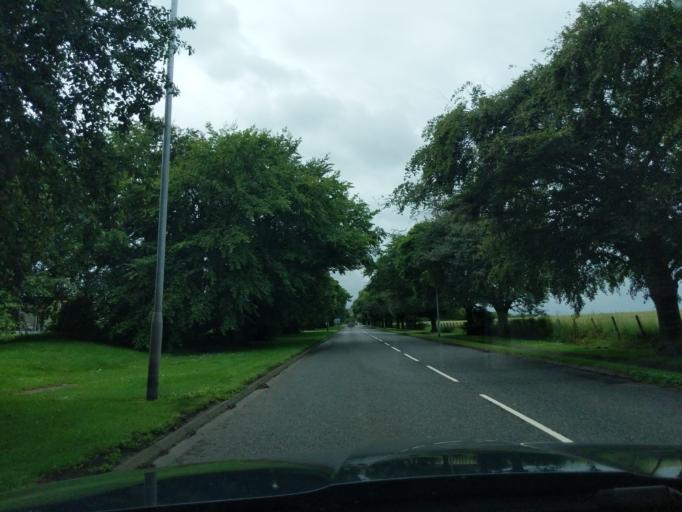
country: GB
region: England
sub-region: Northumberland
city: Berwick-Upon-Tweed
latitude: 55.7613
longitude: -2.0261
